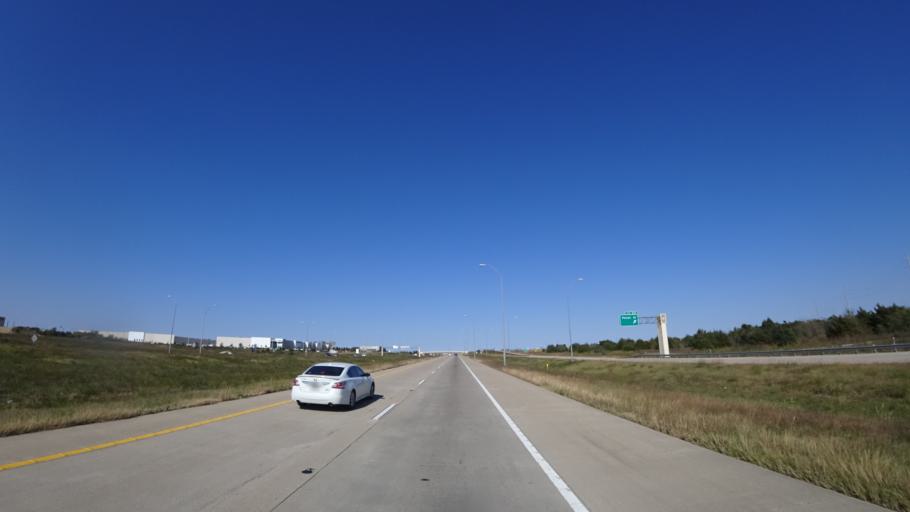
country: US
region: Texas
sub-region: Travis County
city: Pflugerville
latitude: 30.4164
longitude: -97.5858
